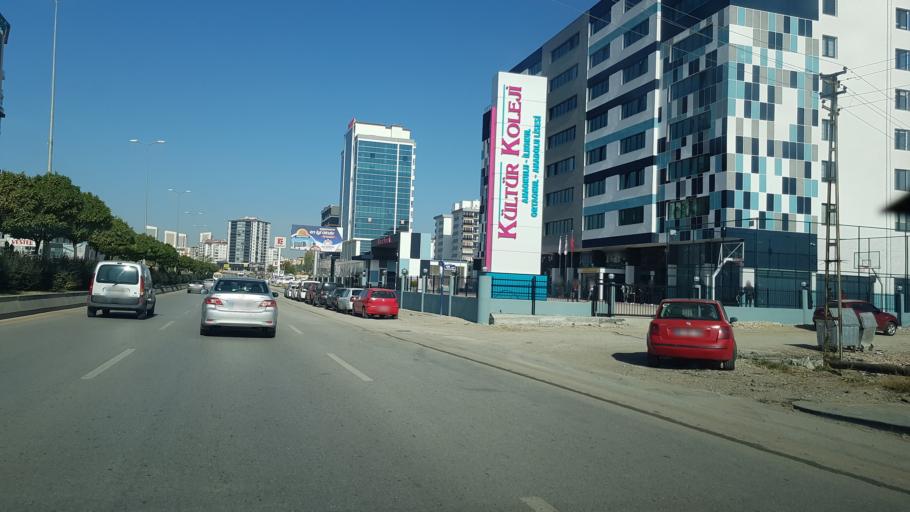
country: TR
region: Ankara
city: Etimesgut
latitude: 39.9654
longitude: 32.6072
